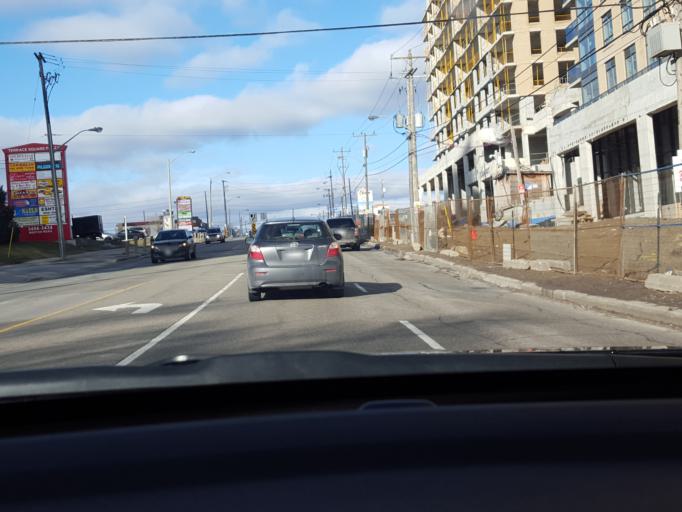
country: CA
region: Ontario
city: Concord
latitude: 43.7496
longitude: -79.5418
